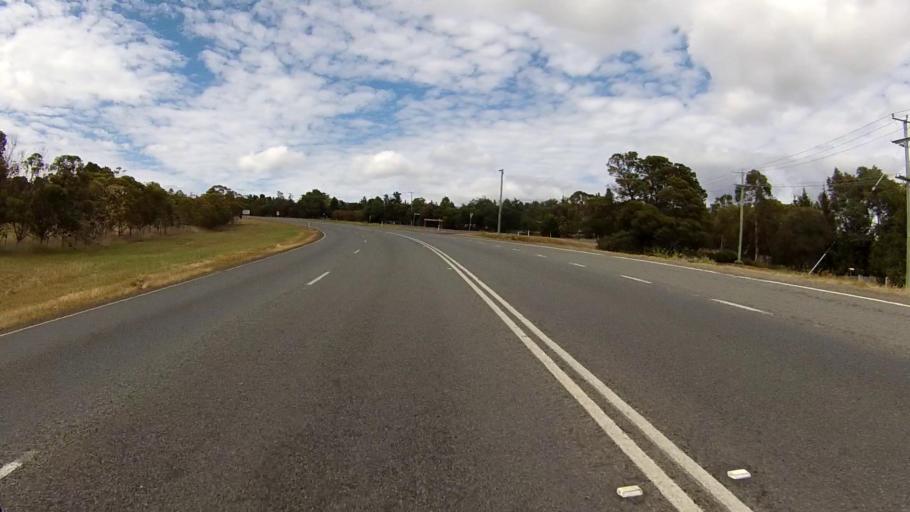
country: AU
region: Tasmania
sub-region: Brighton
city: Old Beach
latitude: -42.7969
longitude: 147.2898
